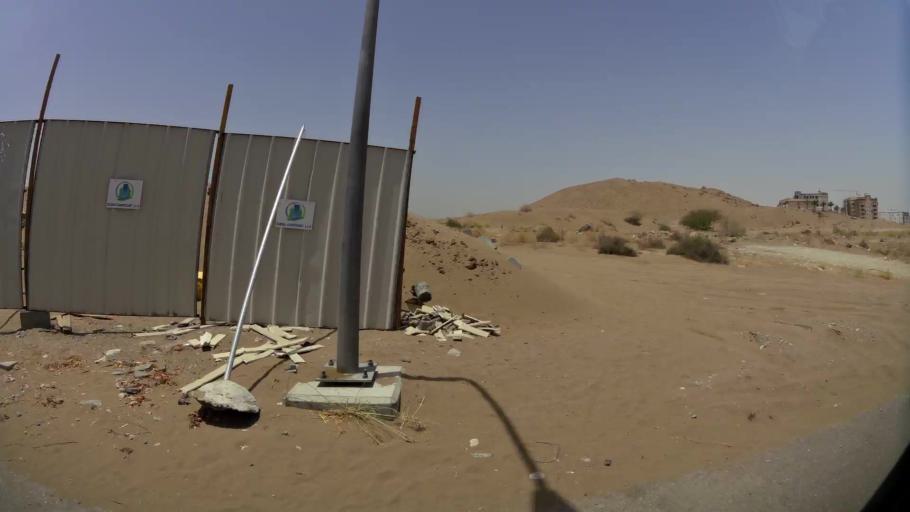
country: OM
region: Muhafazat Masqat
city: Bawshar
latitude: 23.5755
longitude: 58.4258
